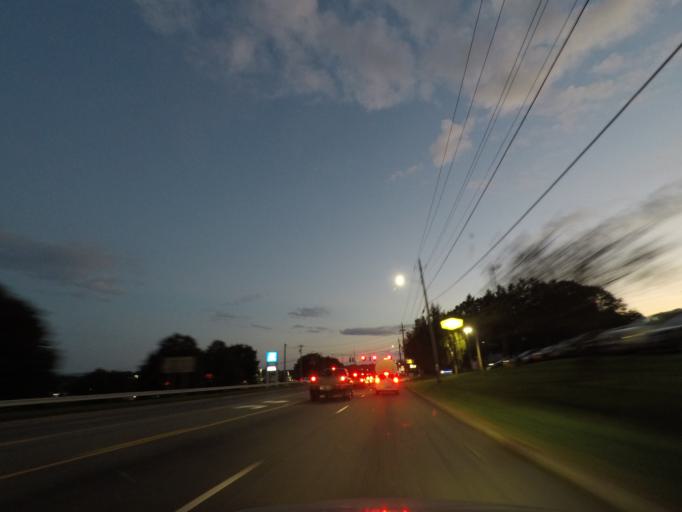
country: US
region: New York
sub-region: Orange County
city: Gardnertown
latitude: 41.5072
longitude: -74.0683
